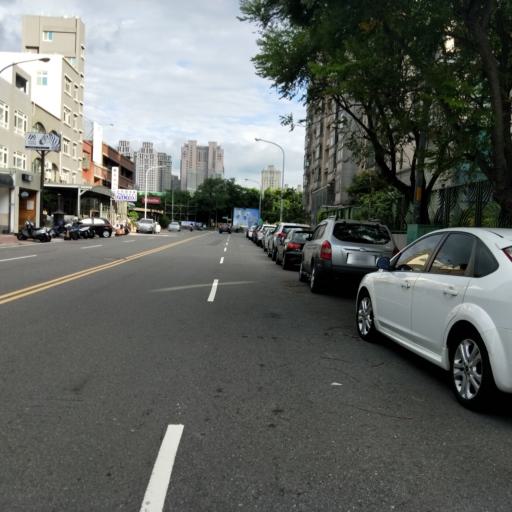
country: TW
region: Taiwan
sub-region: Hsinchu
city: Zhubei
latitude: 24.8294
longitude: 121.0187
